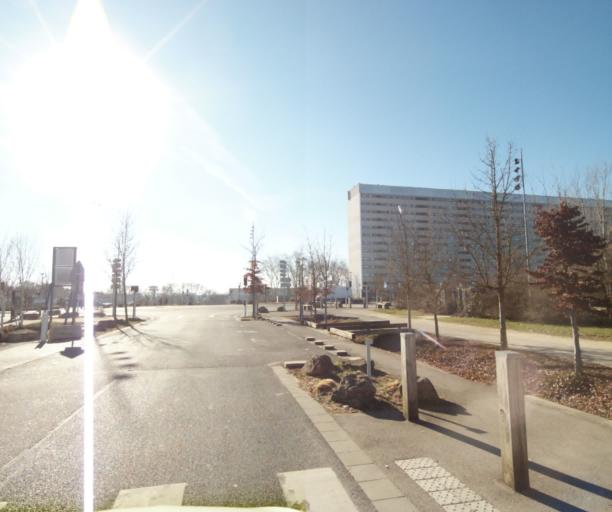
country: FR
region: Lorraine
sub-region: Departement de Meurthe-et-Moselle
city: Maxeville
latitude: 48.7026
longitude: 6.1514
